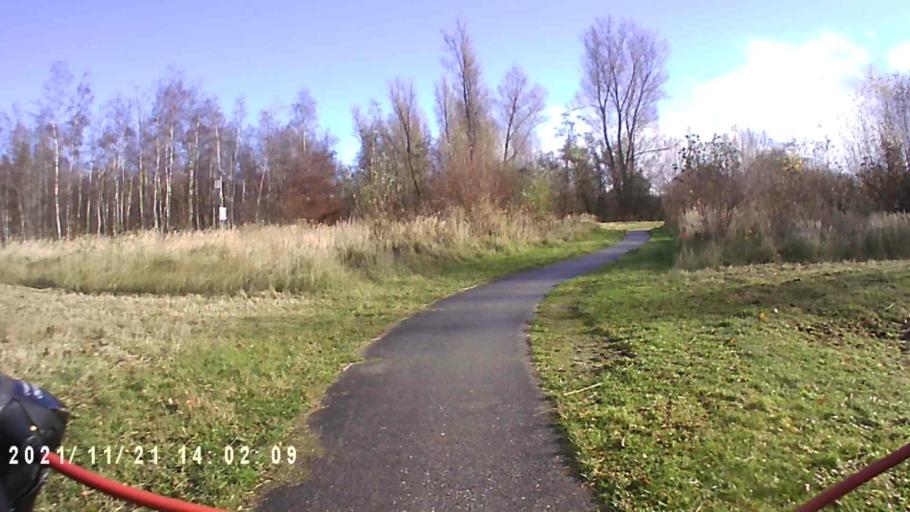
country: NL
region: Groningen
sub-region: Gemeente De Marne
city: Ulrum
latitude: 53.3927
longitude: 6.2414
